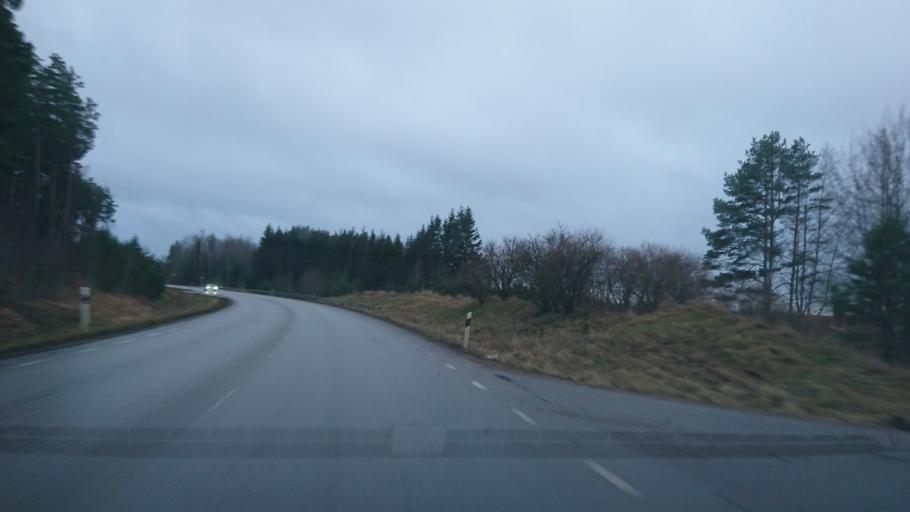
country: SE
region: Uppsala
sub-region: Osthammars Kommun
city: Bjorklinge
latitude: 60.0128
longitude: 17.5874
